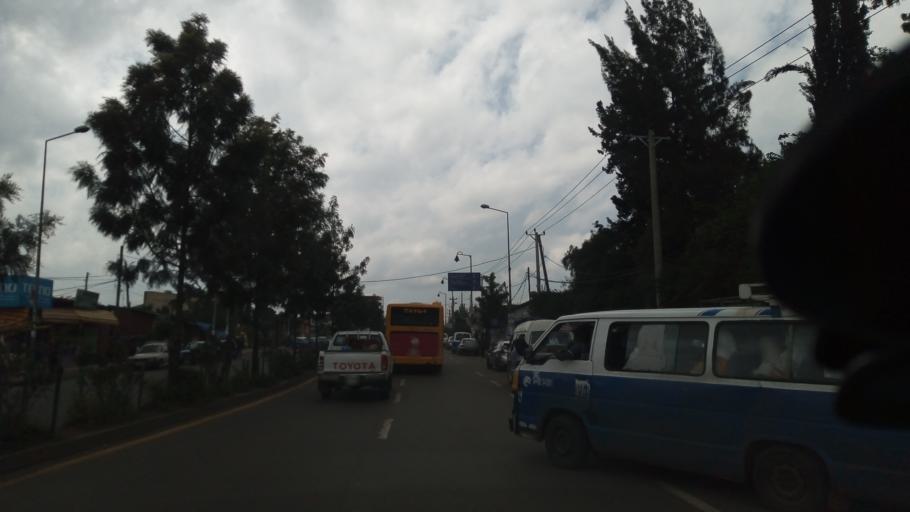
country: ET
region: Adis Abeba
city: Addis Ababa
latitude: 8.9923
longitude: 38.7176
